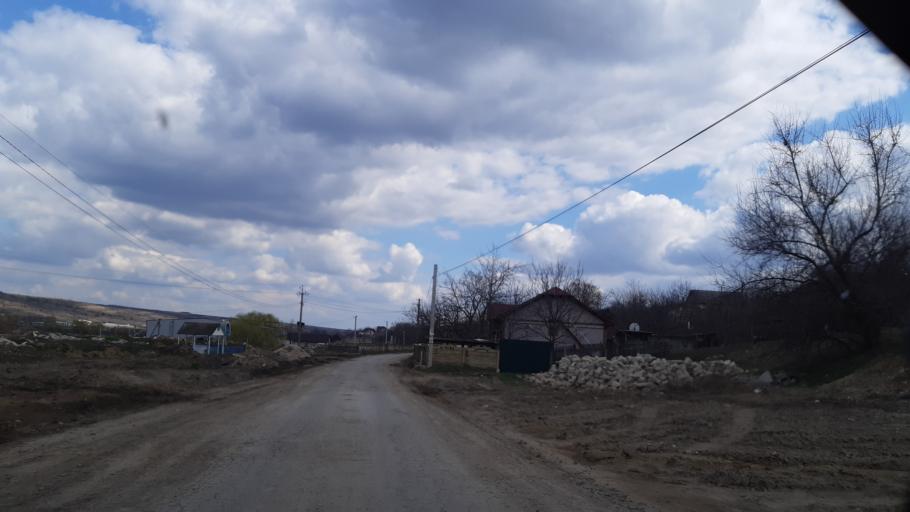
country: MD
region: Laloveni
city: Ialoveni
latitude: 46.8768
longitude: 28.7509
